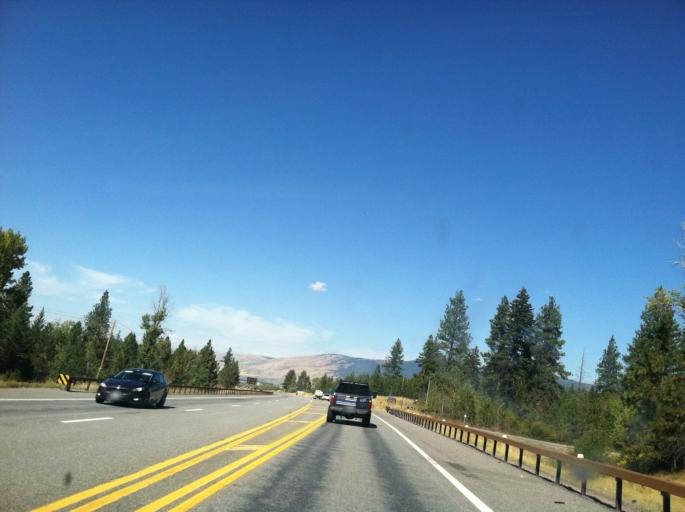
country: US
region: Montana
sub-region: Missoula County
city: Frenchtown
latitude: 47.0922
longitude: -114.0405
